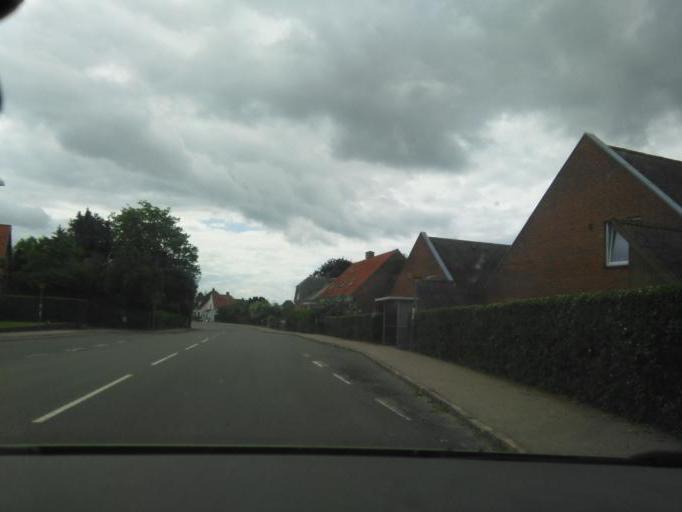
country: DK
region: Zealand
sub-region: Kalundborg Kommune
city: Gorlev
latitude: 55.5430
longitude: 11.2231
